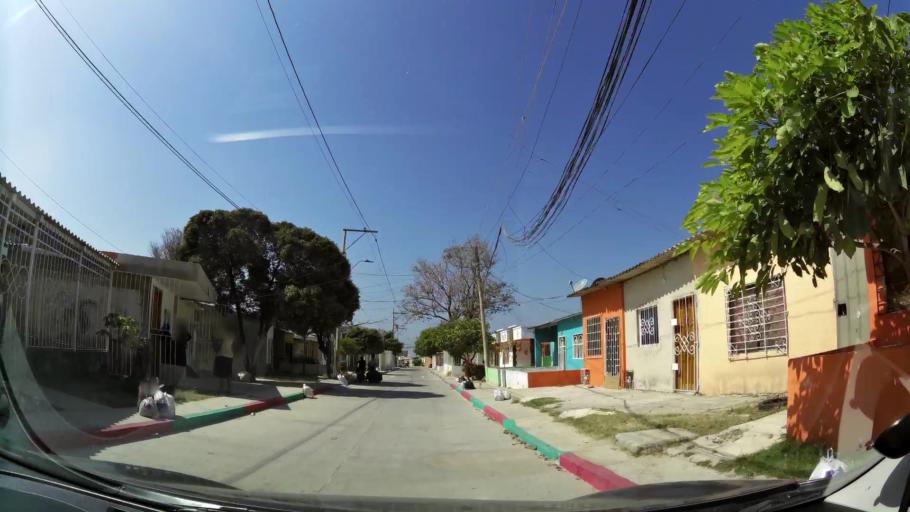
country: CO
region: Atlantico
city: Barranquilla
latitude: 10.9723
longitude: -74.8353
